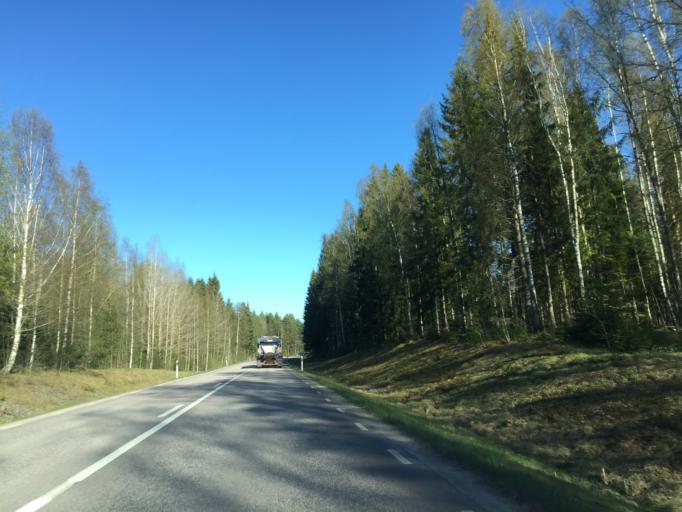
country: SE
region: OErebro
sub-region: Hallsbergs Kommun
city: Skollersta
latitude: 59.2514
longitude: 15.3837
